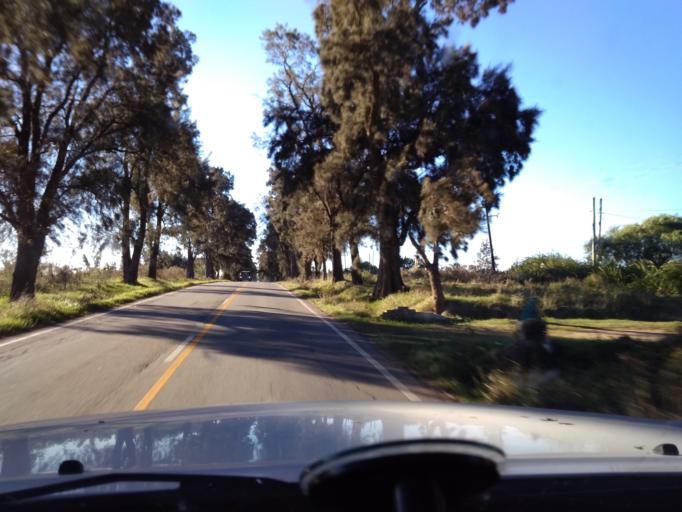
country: UY
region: Canelones
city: San Bautista
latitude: -34.3717
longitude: -55.9594
